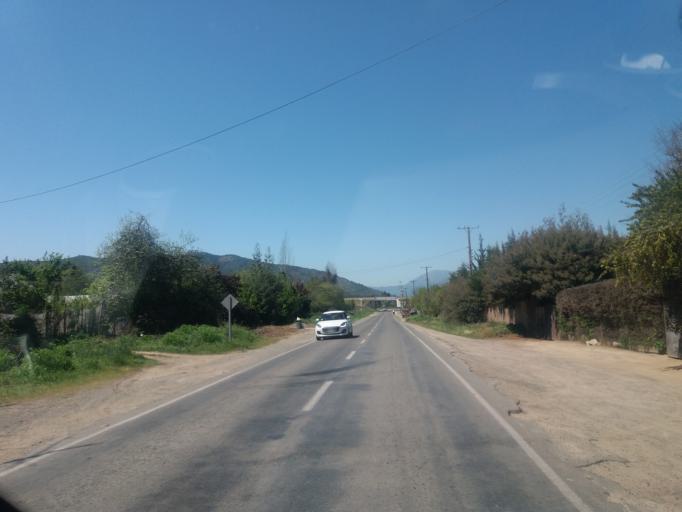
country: CL
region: Valparaiso
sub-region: Provincia de Marga Marga
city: Limache
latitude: -32.9705
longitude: -71.3043
